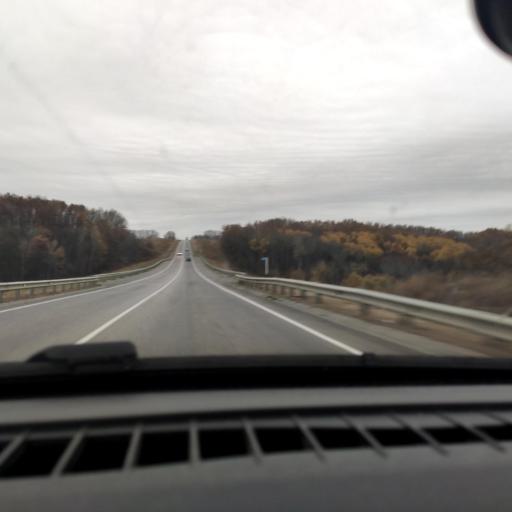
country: RU
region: Voronezj
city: Strelitsa
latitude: 51.5214
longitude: 38.9681
